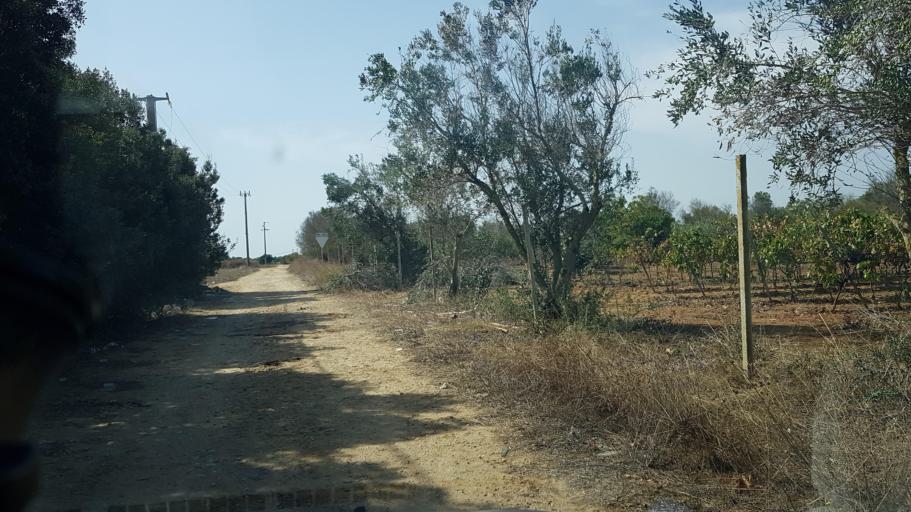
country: IT
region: Apulia
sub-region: Provincia di Brindisi
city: Mesagne
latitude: 40.5864
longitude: 17.8602
